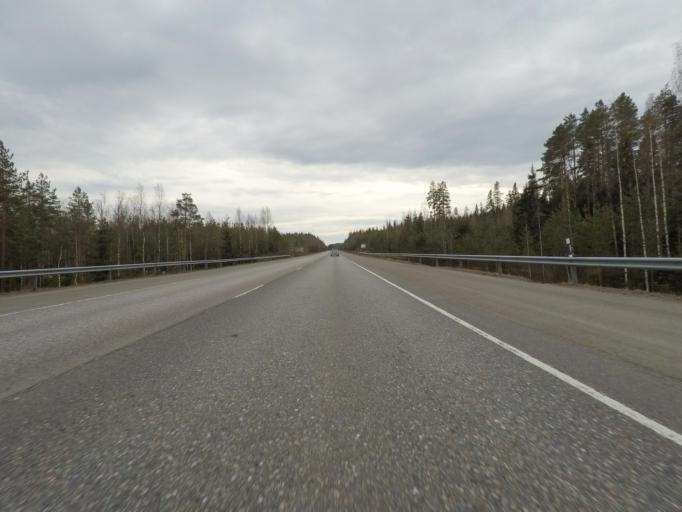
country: FI
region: Paijanne Tavastia
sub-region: Lahti
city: Heinola
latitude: 61.3206
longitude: 26.0424
